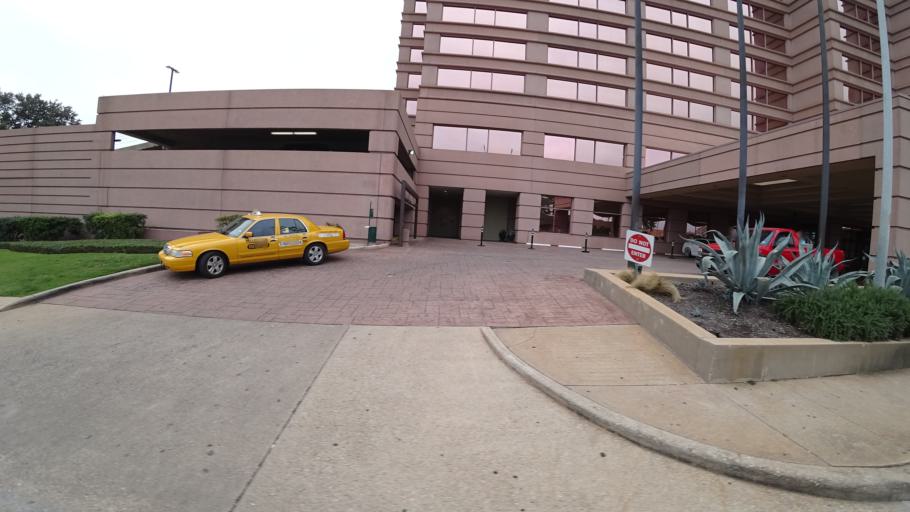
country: US
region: Texas
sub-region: Travis County
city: Austin
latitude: 30.2707
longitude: -97.7339
